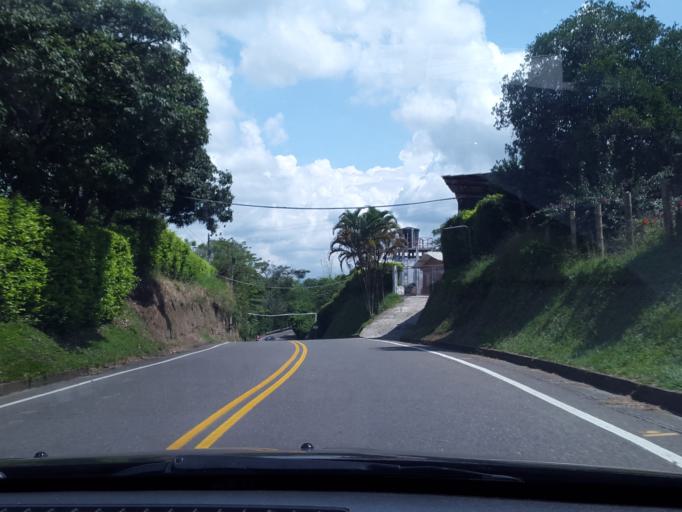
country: CO
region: Valle del Cauca
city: Alcala
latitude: 4.6873
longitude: -75.8165
